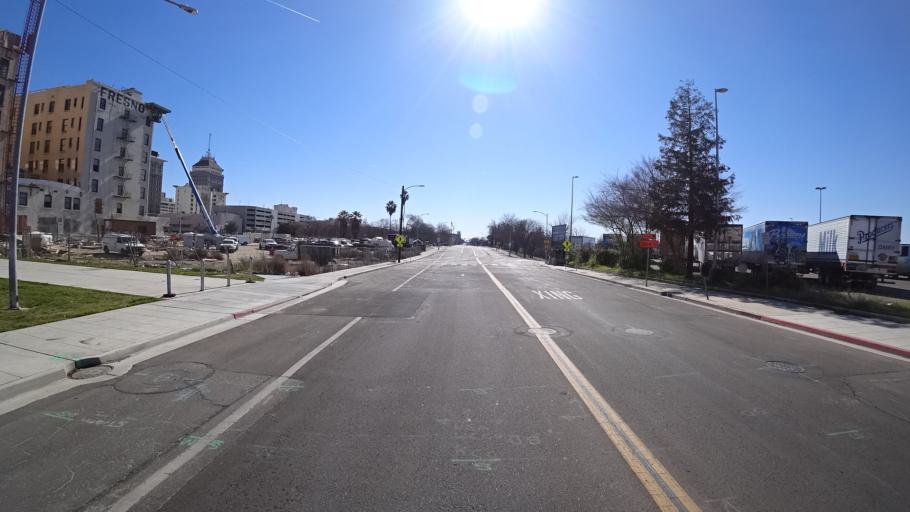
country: US
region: California
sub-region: Fresno County
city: Fresno
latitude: 36.7355
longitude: -119.7955
